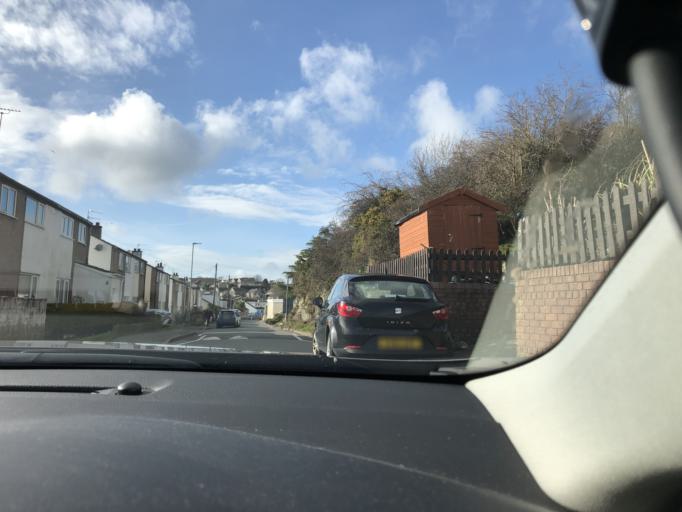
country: GB
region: Wales
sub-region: Anglesey
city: Menai Bridge
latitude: 53.2302
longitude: -4.1679
